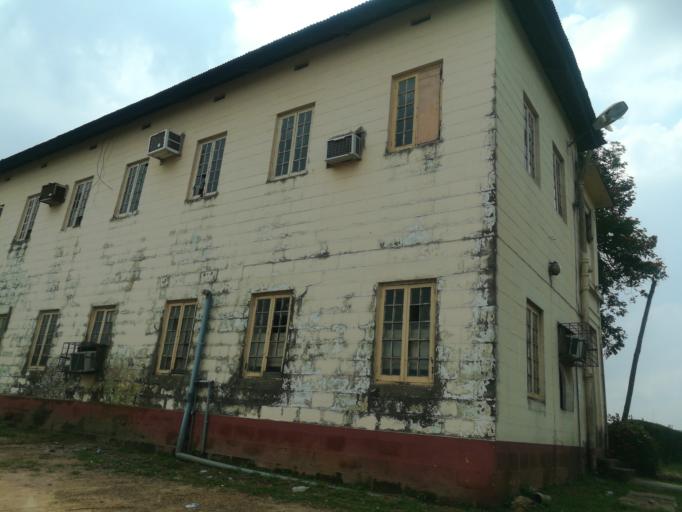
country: NG
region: Oyo
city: Ibadan
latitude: 7.4101
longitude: 3.9081
